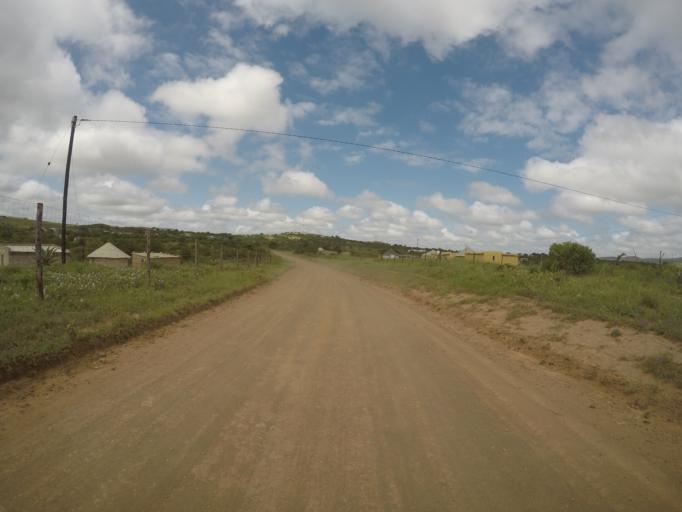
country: ZA
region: KwaZulu-Natal
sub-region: uThungulu District Municipality
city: Empangeni
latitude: -28.5966
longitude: 31.8384
